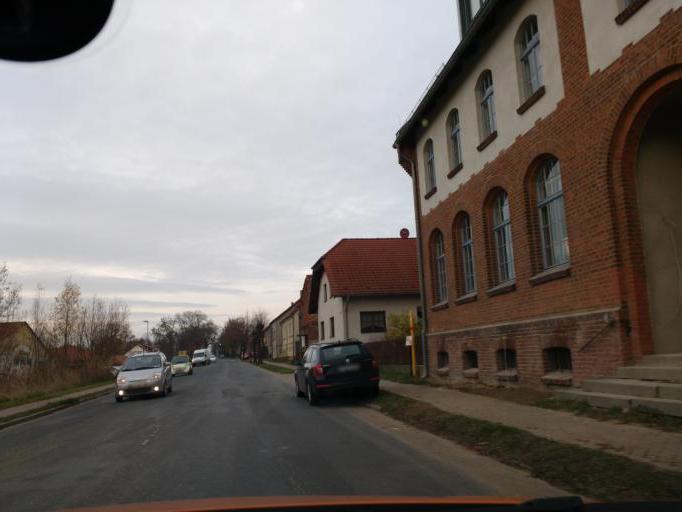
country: DE
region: Brandenburg
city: Velten
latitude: 52.7183
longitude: 13.1002
